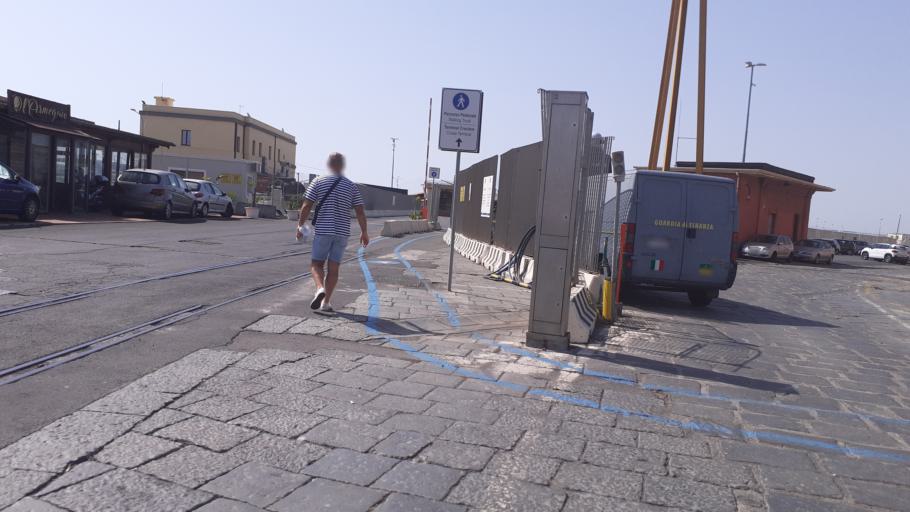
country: IT
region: Sicily
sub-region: Catania
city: Catania
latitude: 37.4988
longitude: 15.0946
